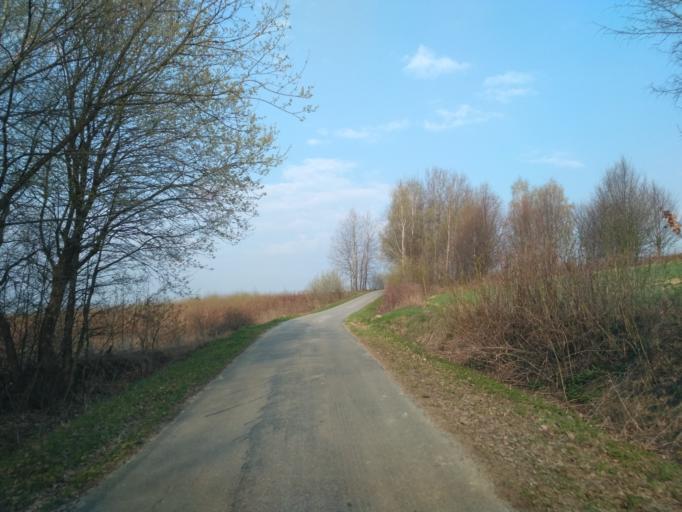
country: PL
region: Subcarpathian Voivodeship
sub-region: Powiat strzyzowski
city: Wisniowa
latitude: 49.8898
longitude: 21.6250
